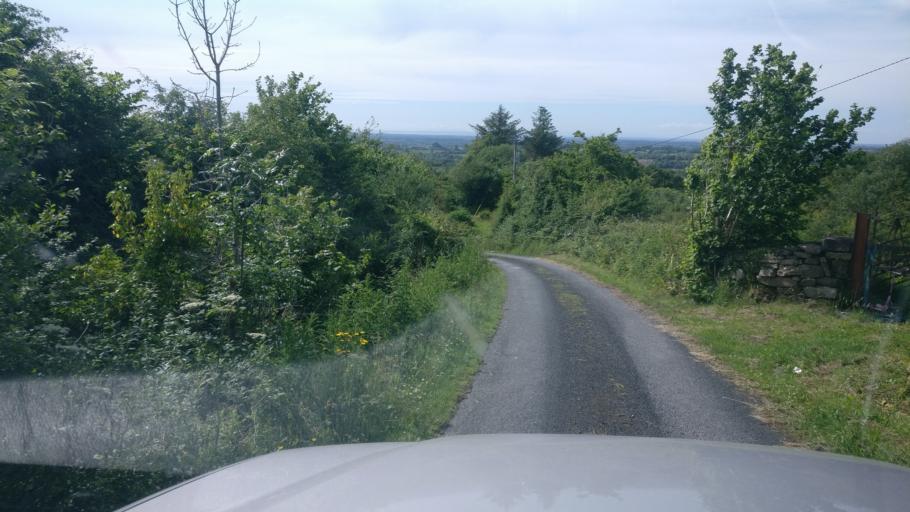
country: IE
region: Connaught
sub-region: County Galway
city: Gort
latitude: 53.0918
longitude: -8.6968
